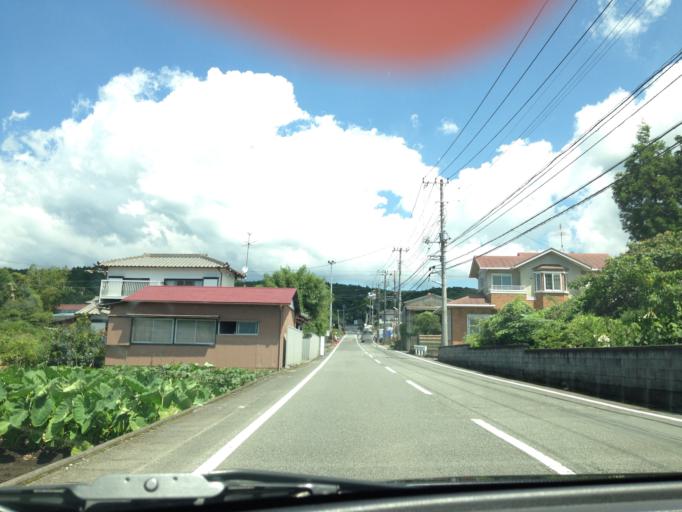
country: JP
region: Shizuoka
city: Fuji
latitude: 35.2042
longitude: 138.7218
